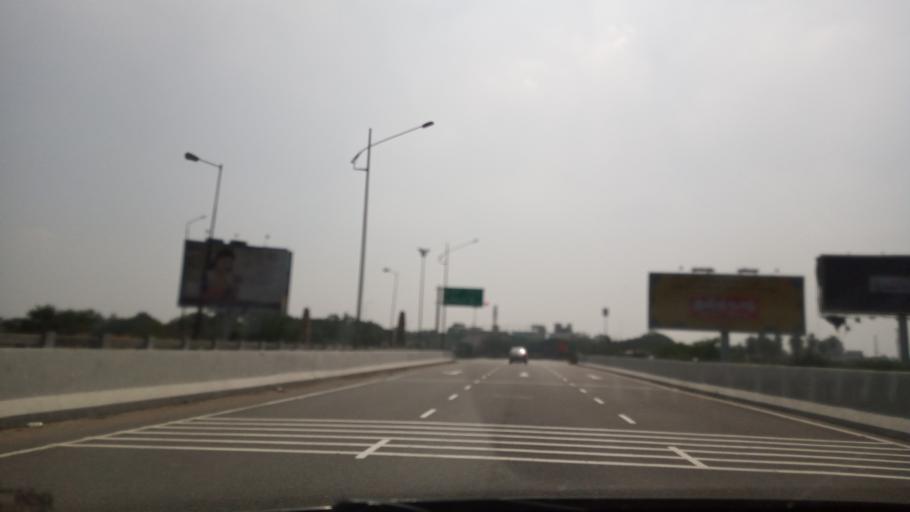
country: IN
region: Tamil Nadu
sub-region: Vellore
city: Arcot
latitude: 12.9143
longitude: 79.3273
